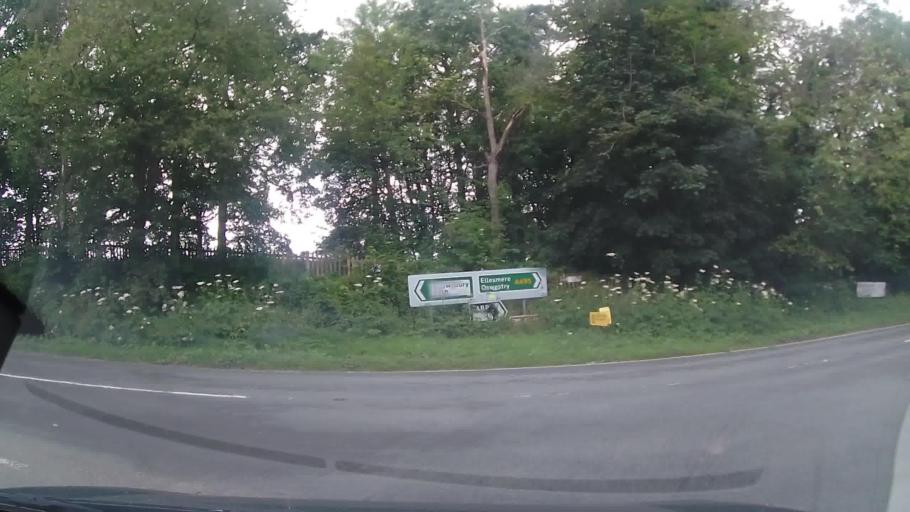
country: GB
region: England
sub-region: Shropshire
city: Ellesmere
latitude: 52.8999
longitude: -2.8751
